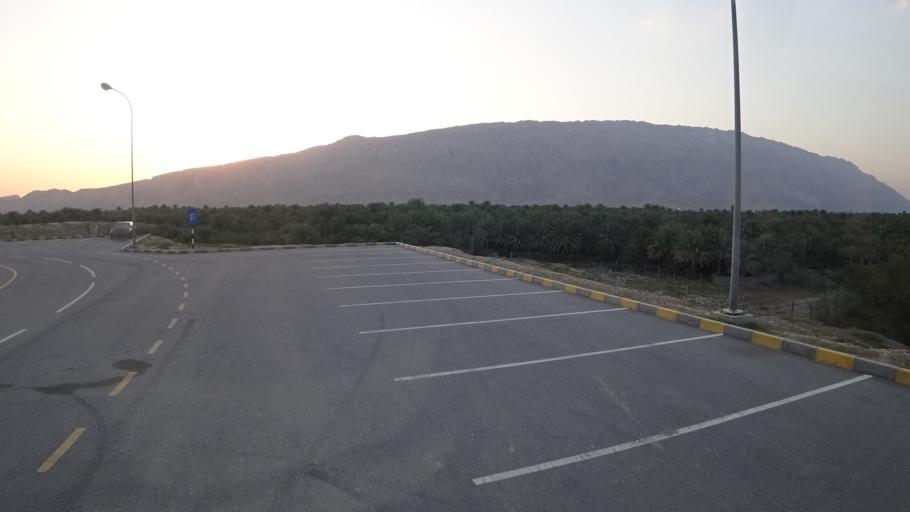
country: AE
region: Abu Dhabi
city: Al Ain
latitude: 23.9813
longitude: 55.8366
